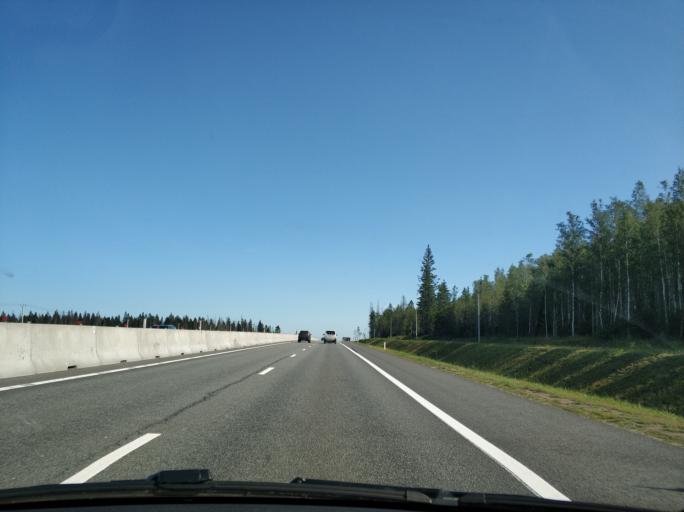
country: RU
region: Leningrad
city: Sosnovo
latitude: 60.4887
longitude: 30.1958
